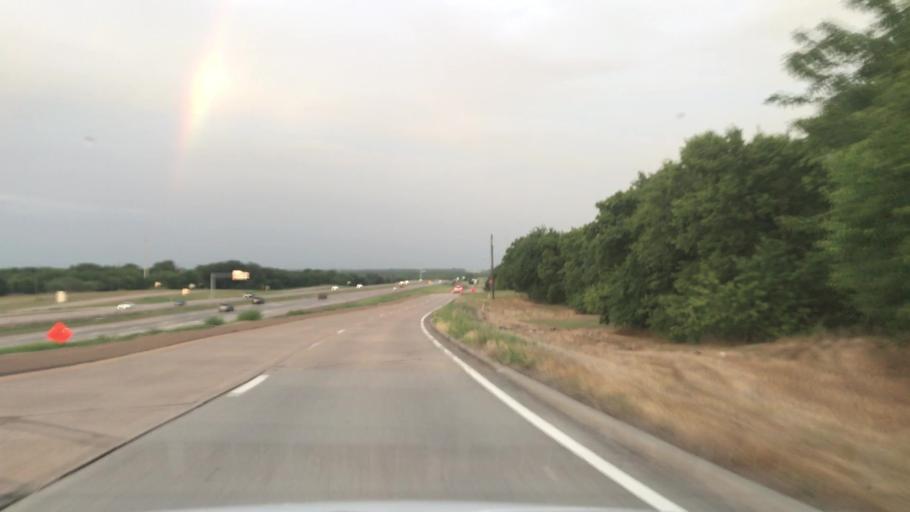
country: US
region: Texas
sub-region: Dallas County
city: Balch Springs
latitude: 32.7029
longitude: -96.5661
